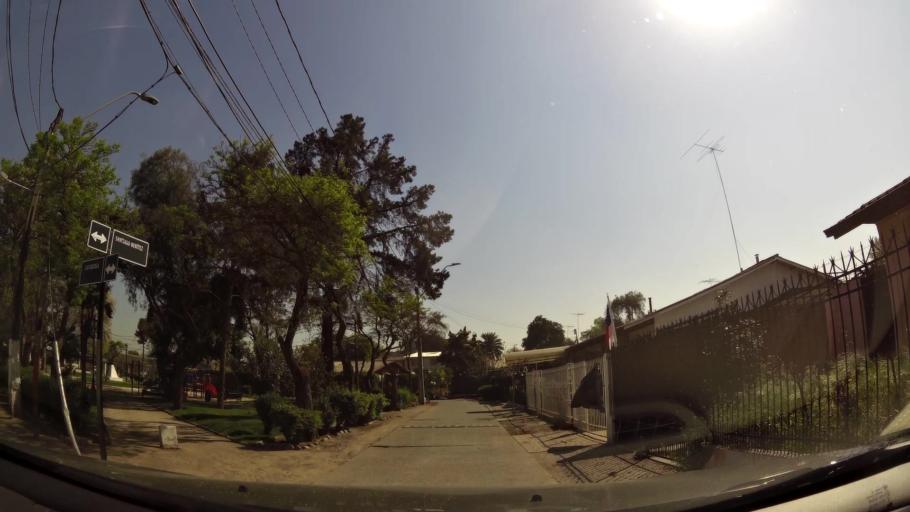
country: CL
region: Santiago Metropolitan
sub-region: Provincia de Maipo
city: San Bernardo
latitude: -33.5890
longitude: -70.6991
